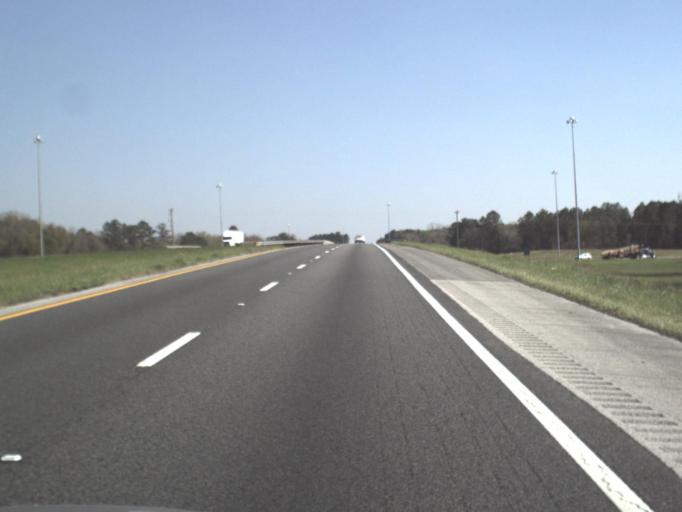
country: US
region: Florida
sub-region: Jackson County
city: Sneads
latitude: 30.6581
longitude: -85.0401
